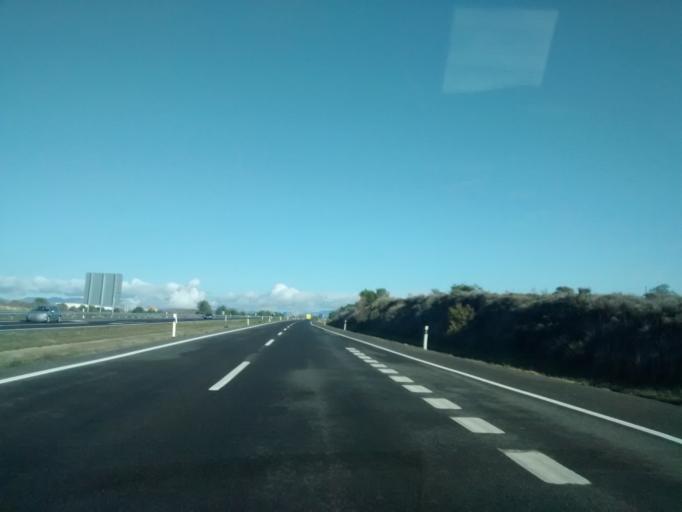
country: ES
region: Aragon
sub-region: Provincia de Huesca
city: Almudebar
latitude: 42.0376
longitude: -0.5710
